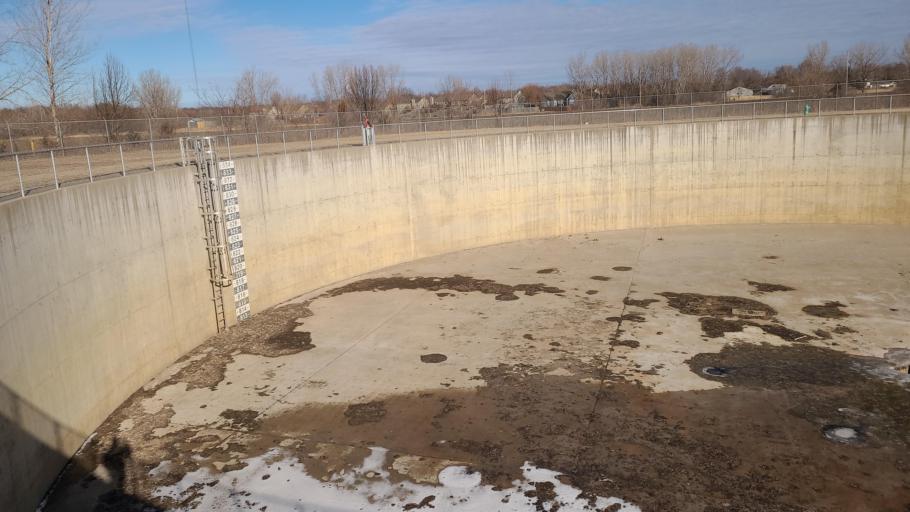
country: US
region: Kansas
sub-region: Douglas County
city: Lawrence
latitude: 38.9325
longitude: -95.2856
